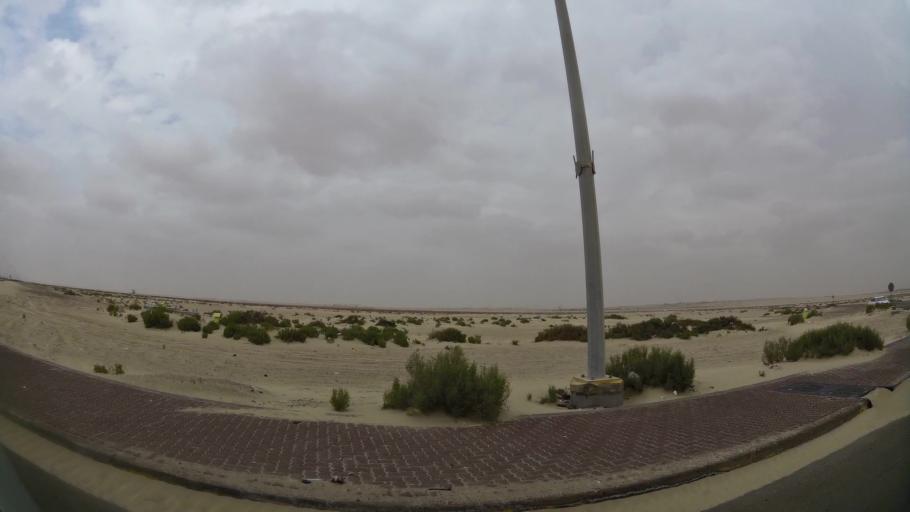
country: AE
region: Abu Dhabi
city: Abu Dhabi
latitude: 24.3317
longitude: 54.6492
